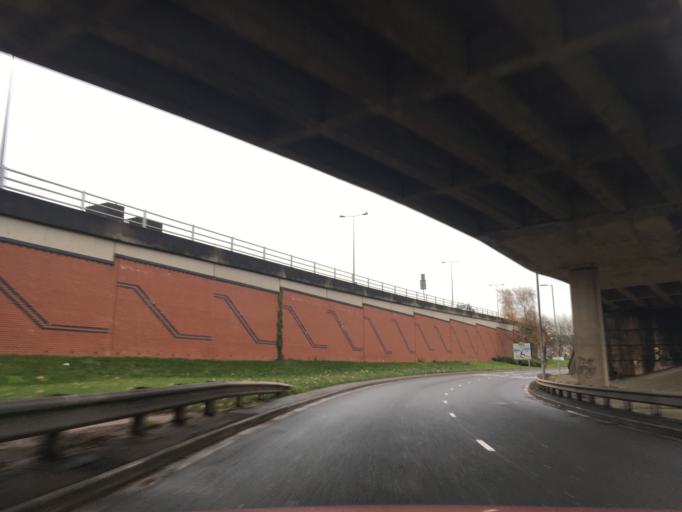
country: GB
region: Wales
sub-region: Newport
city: Newport
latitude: 51.5928
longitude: -2.9967
